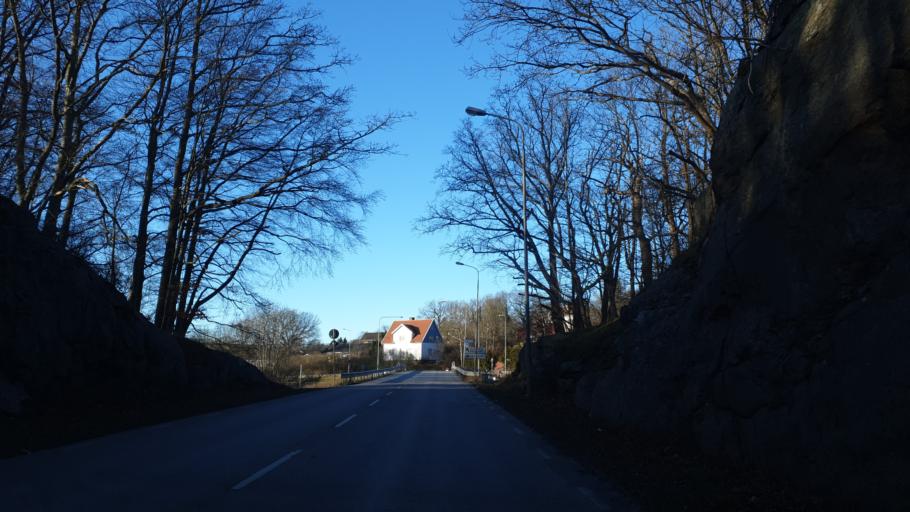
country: SE
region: Blekinge
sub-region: Karlskrona Kommun
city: Rodeby
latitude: 56.2042
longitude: 15.6336
